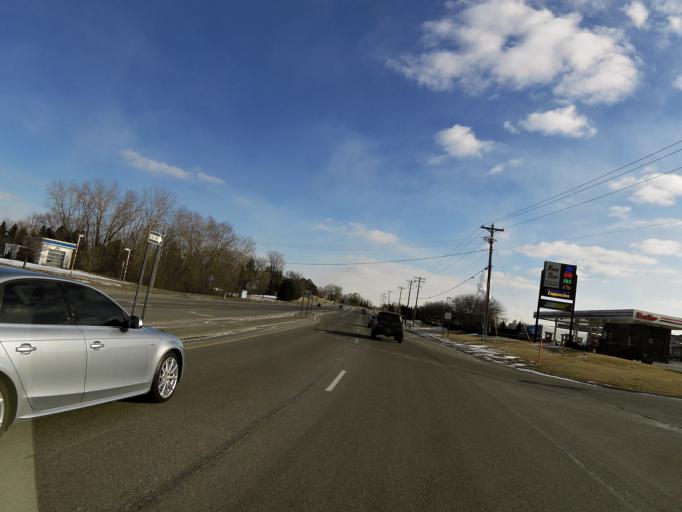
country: US
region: Minnesota
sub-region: Dakota County
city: Mendota Heights
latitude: 44.8448
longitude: -93.1238
